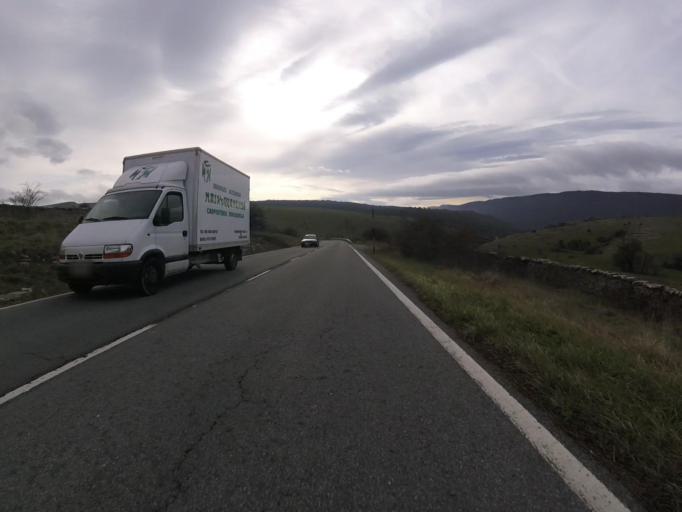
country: ES
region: Navarre
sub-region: Provincia de Navarra
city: Lezaun
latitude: 42.8463
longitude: -2.0158
